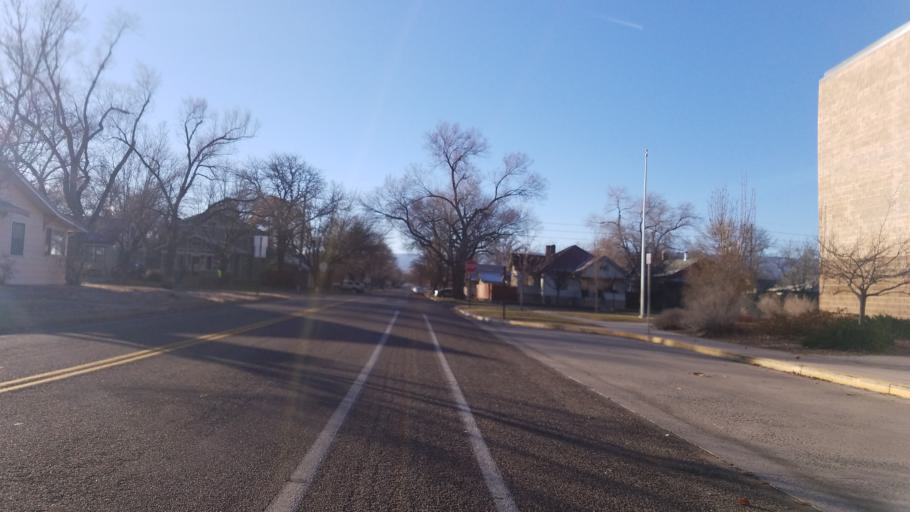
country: US
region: Colorado
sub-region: Mesa County
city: Grand Junction
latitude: 39.0729
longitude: -108.5560
